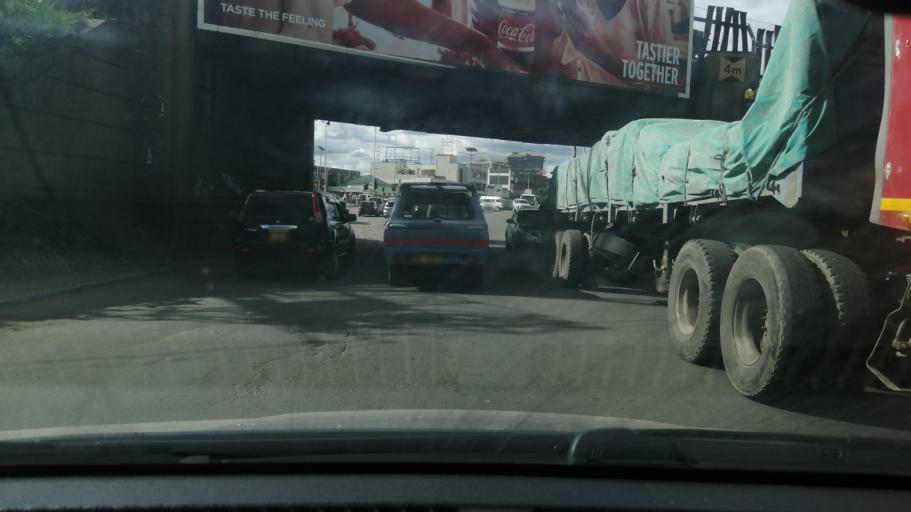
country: ZW
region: Harare
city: Harare
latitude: -17.8371
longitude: 31.0472
